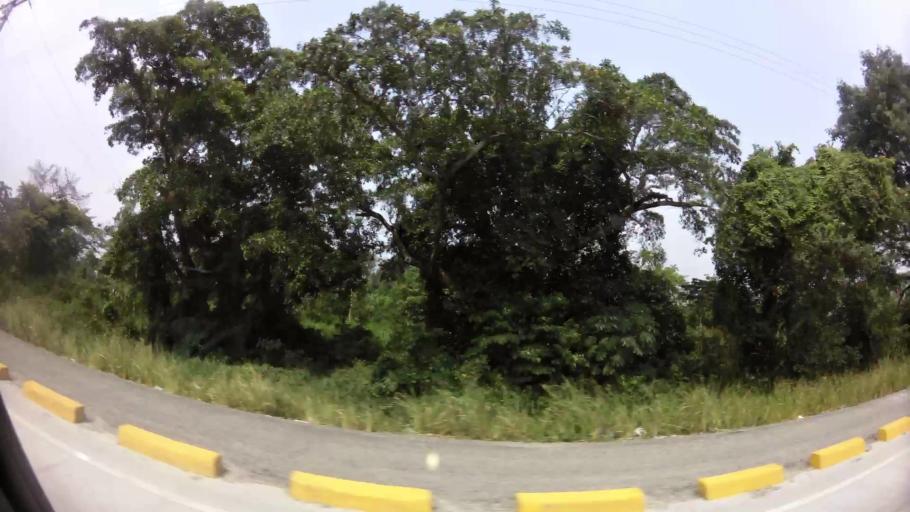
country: HN
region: Cortes
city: San Pedro Sula
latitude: 15.5267
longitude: -88.0046
